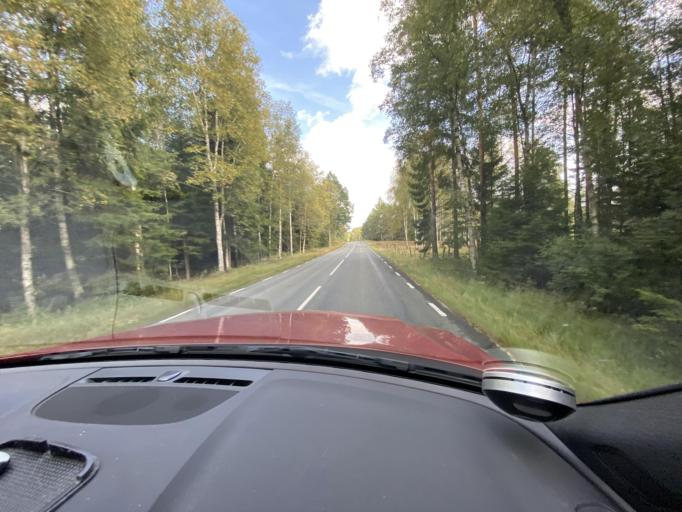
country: SE
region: Skane
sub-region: Hassleholms Kommun
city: Bjarnum
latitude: 56.3547
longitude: 13.7604
